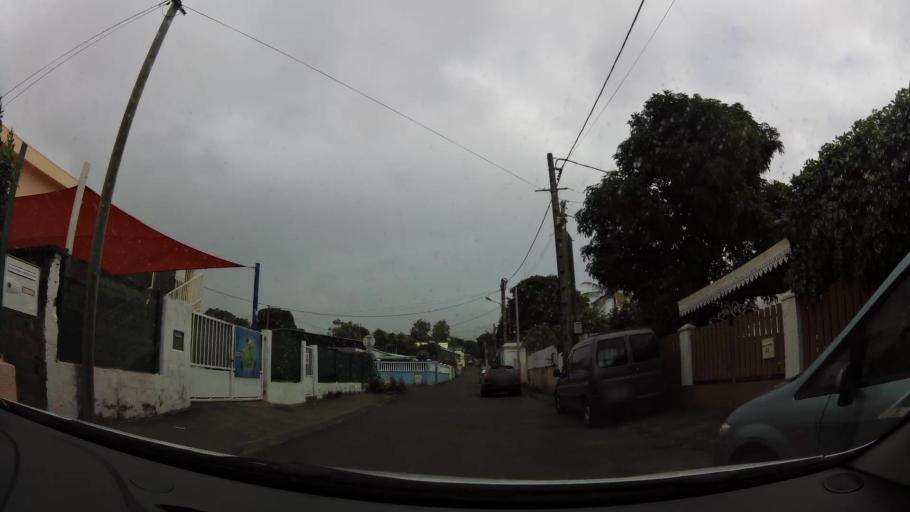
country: RE
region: Reunion
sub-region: Reunion
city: Sainte-Marie
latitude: -20.9000
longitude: 55.5481
